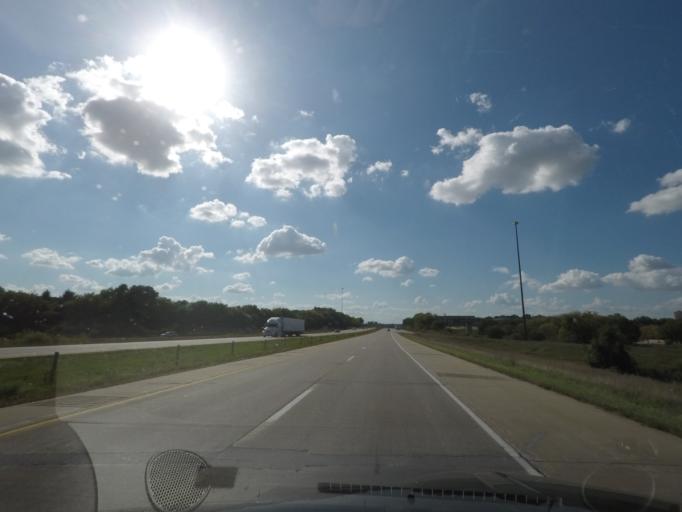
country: US
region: Iowa
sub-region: Polk County
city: Clive
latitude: 41.5923
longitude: -93.7818
